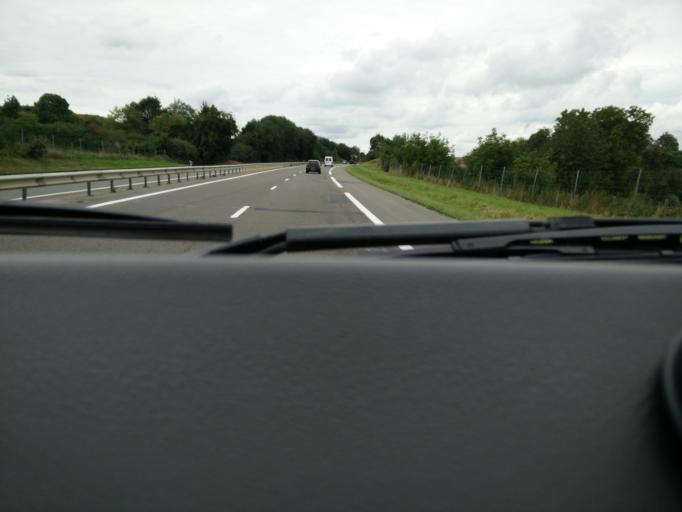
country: FR
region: Champagne-Ardenne
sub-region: Departement des Ardennes
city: Sedan
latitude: 49.6882
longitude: 4.9366
